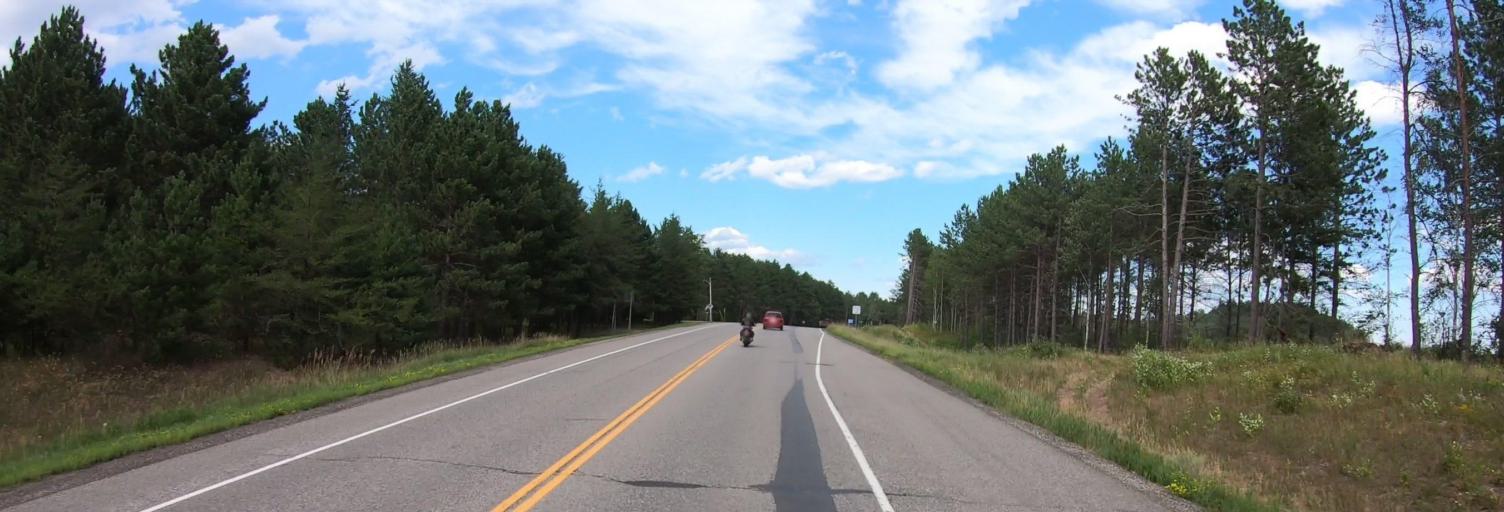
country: US
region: Minnesota
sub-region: Saint Louis County
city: Aurora
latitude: 47.8141
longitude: -92.2285
